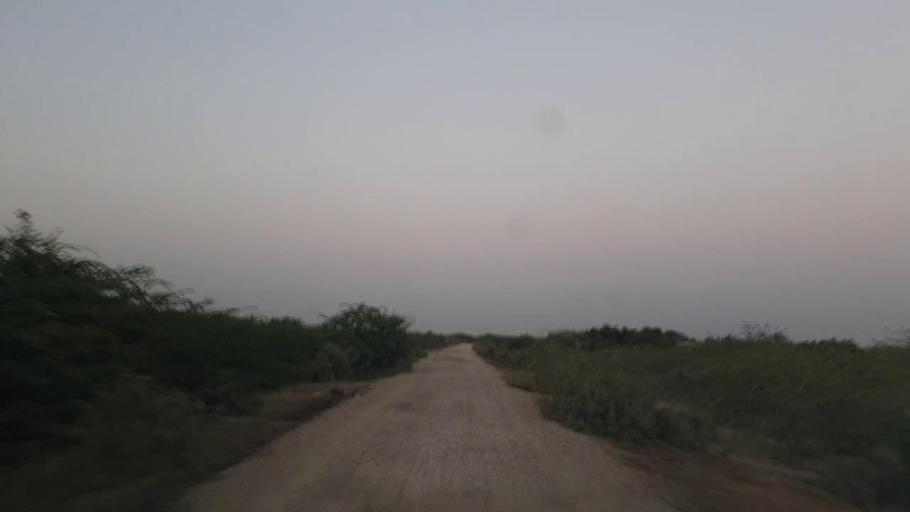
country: PK
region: Sindh
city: Naukot
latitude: 24.7598
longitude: 69.2902
